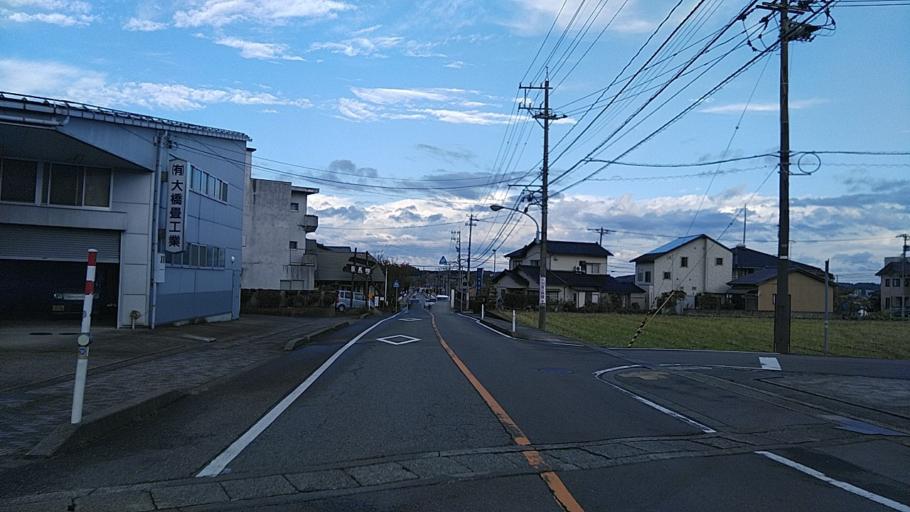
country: JP
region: Ishikawa
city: Komatsu
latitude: 36.2918
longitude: 136.3551
